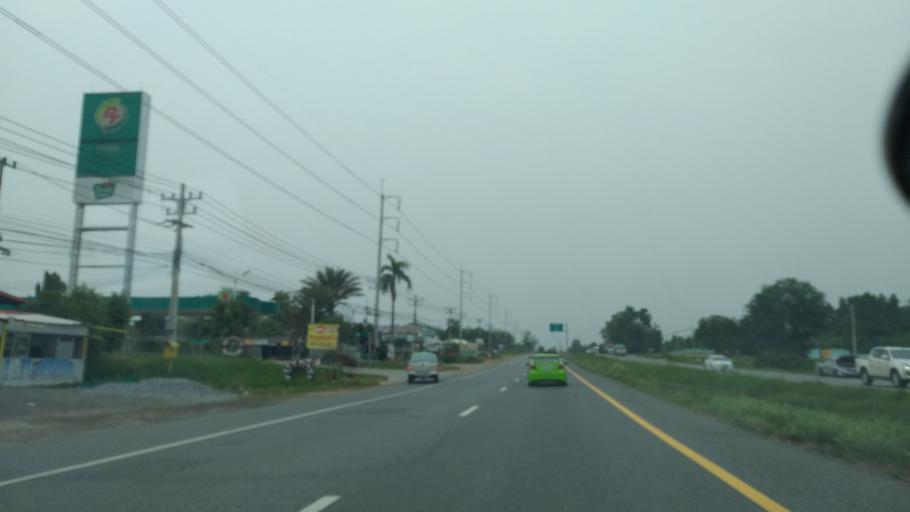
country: TH
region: Chon Buri
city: Ko Chan
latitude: 13.4430
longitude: 101.2833
